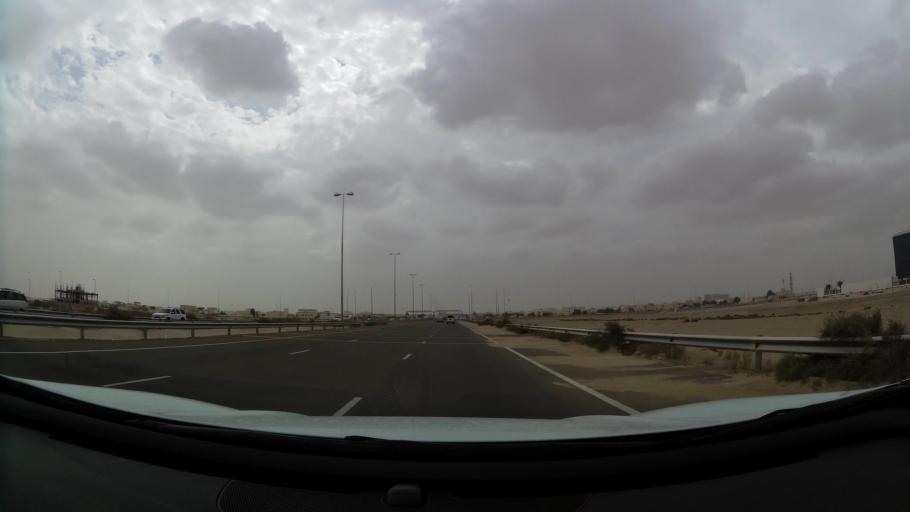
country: AE
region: Abu Dhabi
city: Abu Dhabi
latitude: 24.3380
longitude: 54.6439
